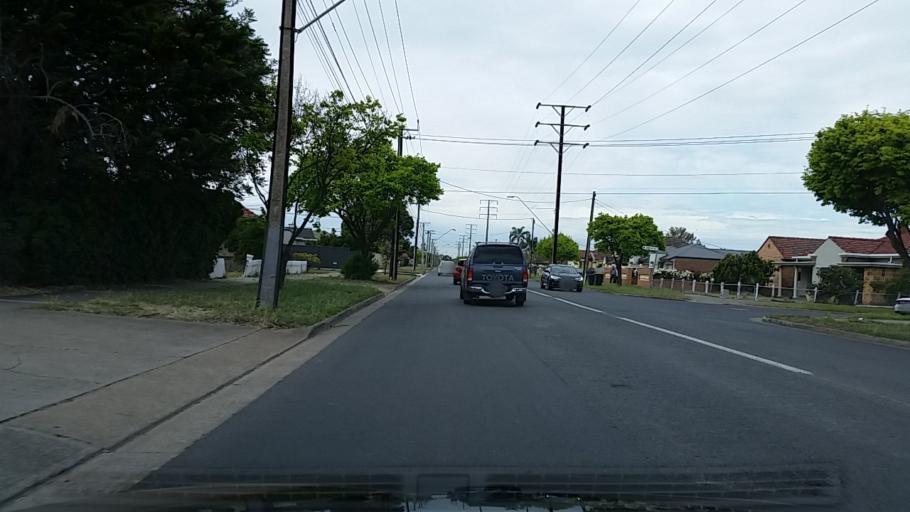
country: AU
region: South Australia
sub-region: Charles Sturt
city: Allenby Gardens
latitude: -34.9103
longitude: 138.5491
